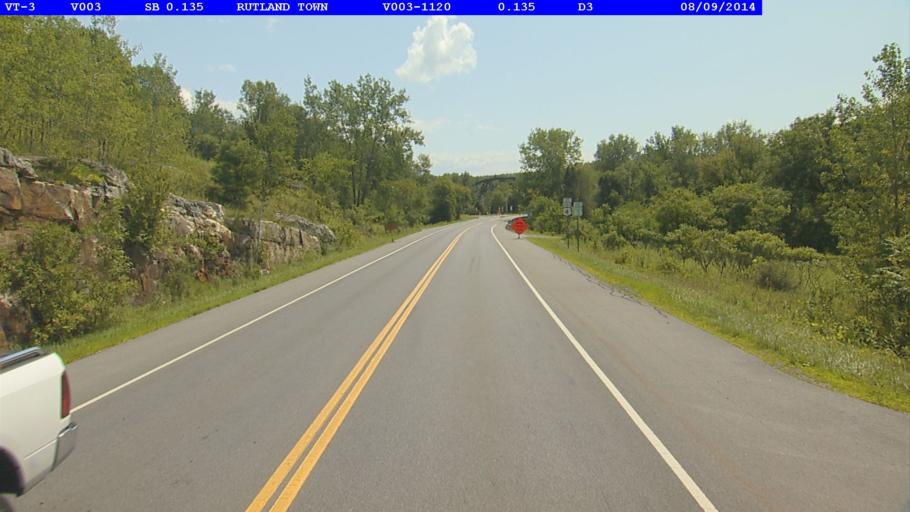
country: US
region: Vermont
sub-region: Rutland County
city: West Rutland
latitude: 43.6059
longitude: -73.0152
